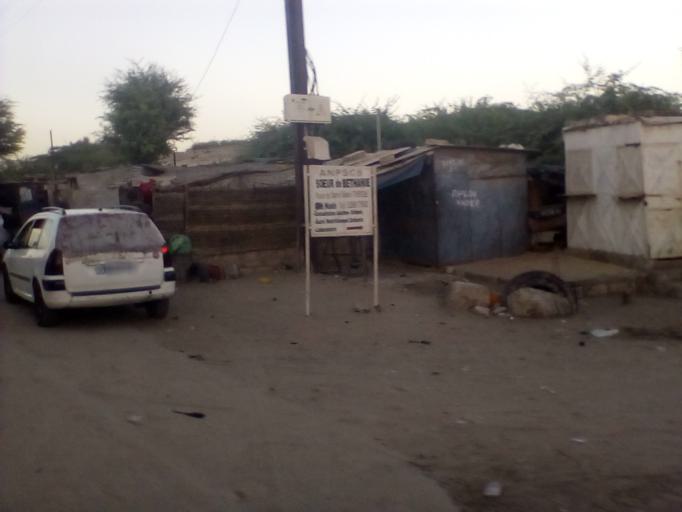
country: SN
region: Saint-Louis
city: Saint-Louis
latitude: 16.0118
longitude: -16.4888
